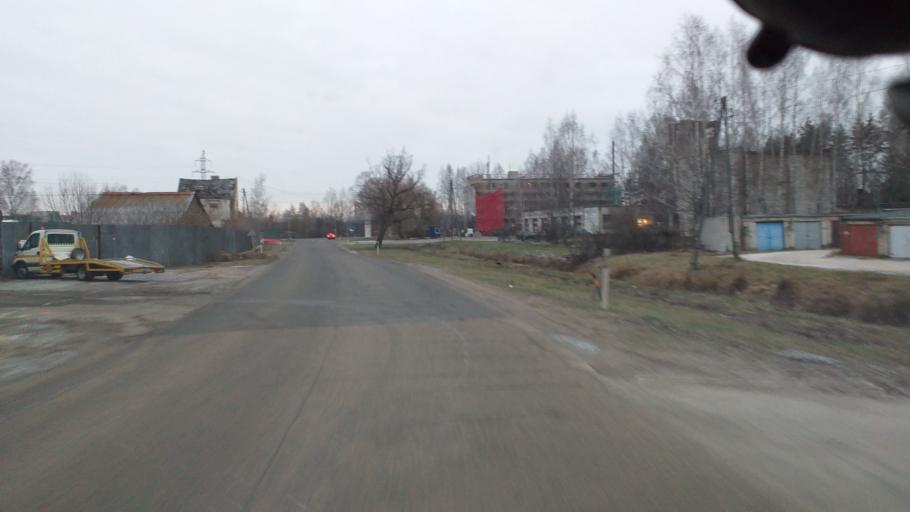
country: LV
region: Olaine
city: Olaine
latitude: 56.7948
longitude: 23.9403
